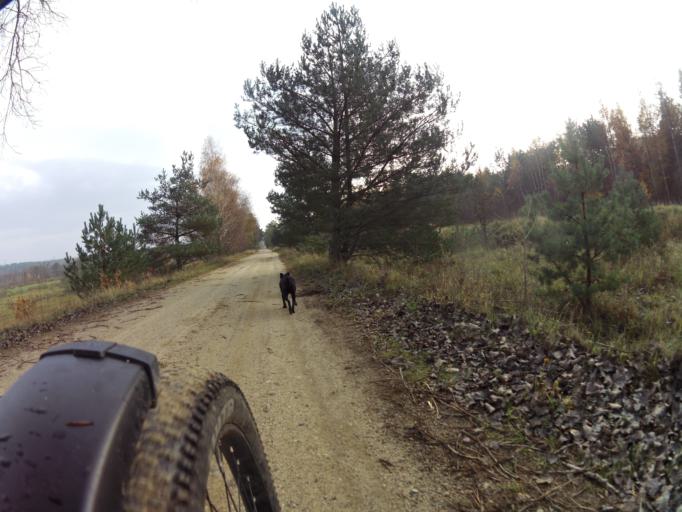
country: PL
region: Pomeranian Voivodeship
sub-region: Powiat wejherowski
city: Orle
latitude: 54.7034
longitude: 18.1064
